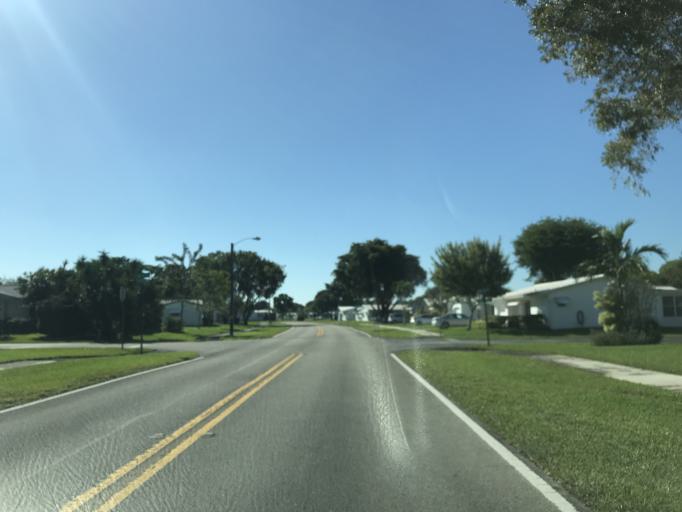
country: US
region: Florida
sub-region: Broward County
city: Plantation
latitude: 26.1422
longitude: -80.2692
